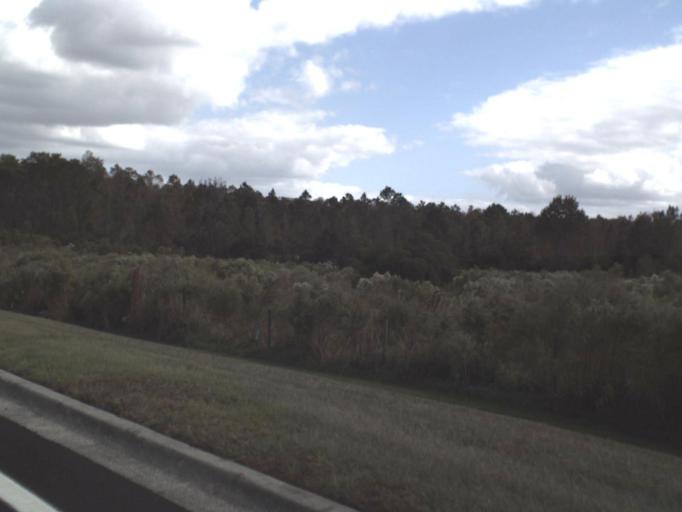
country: US
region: Florida
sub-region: Orange County
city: Hunters Creek
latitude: 28.3457
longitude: -81.4558
